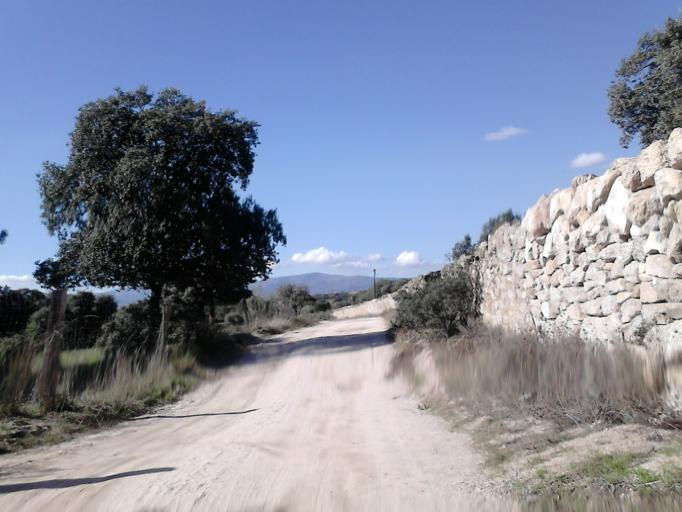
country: ES
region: Madrid
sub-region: Provincia de Madrid
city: Galapagar
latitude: 40.5613
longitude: -3.9910
